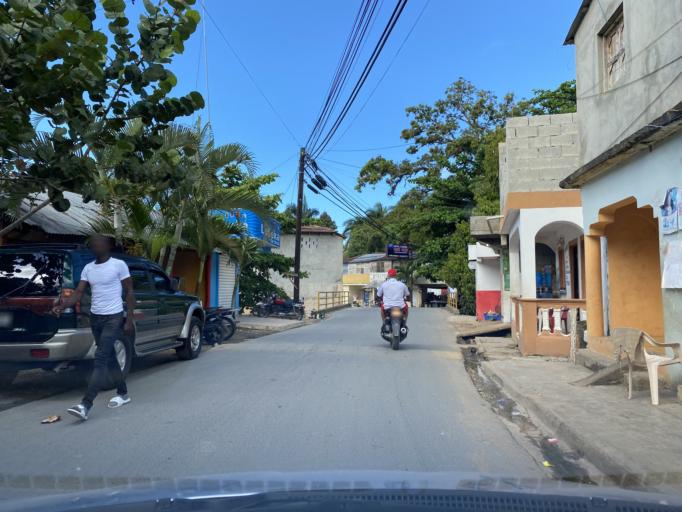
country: DO
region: Samana
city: Las Terrenas
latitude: 19.3096
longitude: -69.5417
